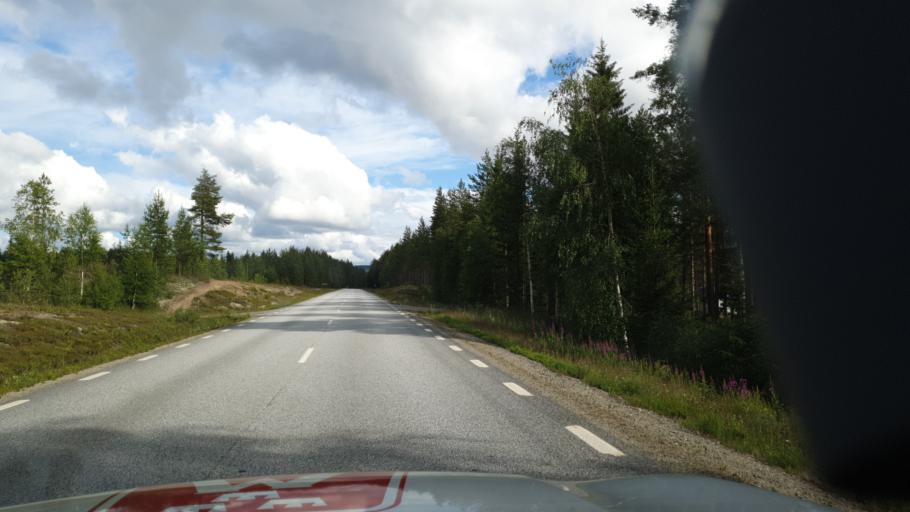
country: SE
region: Vaesterbotten
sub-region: Vindelns Kommun
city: Vindeln
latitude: 64.3743
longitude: 19.4104
